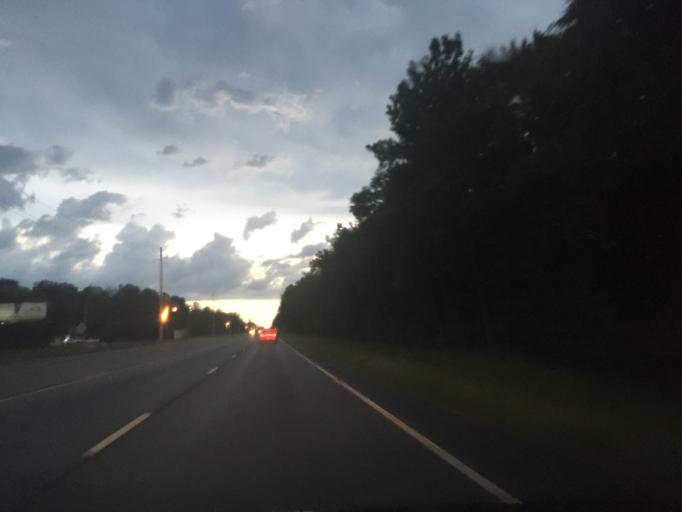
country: US
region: Georgia
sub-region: Liberty County
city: Hinesville
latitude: 31.8535
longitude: -81.5565
